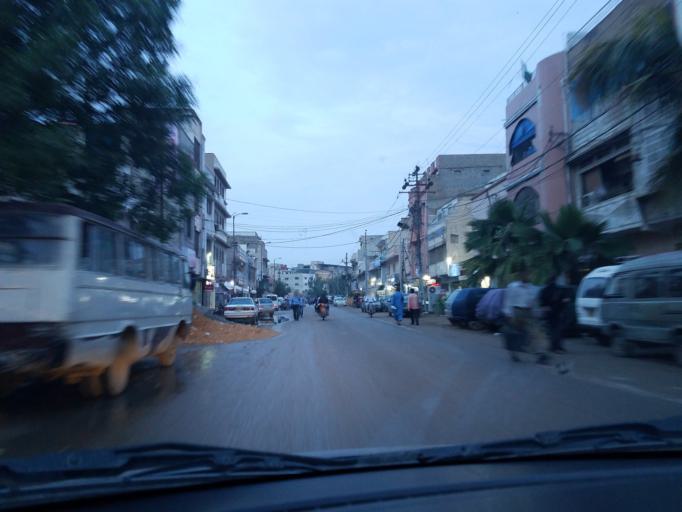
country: PK
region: Sindh
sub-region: Karachi District
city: Karachi
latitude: 24.9485
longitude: 67.0799
